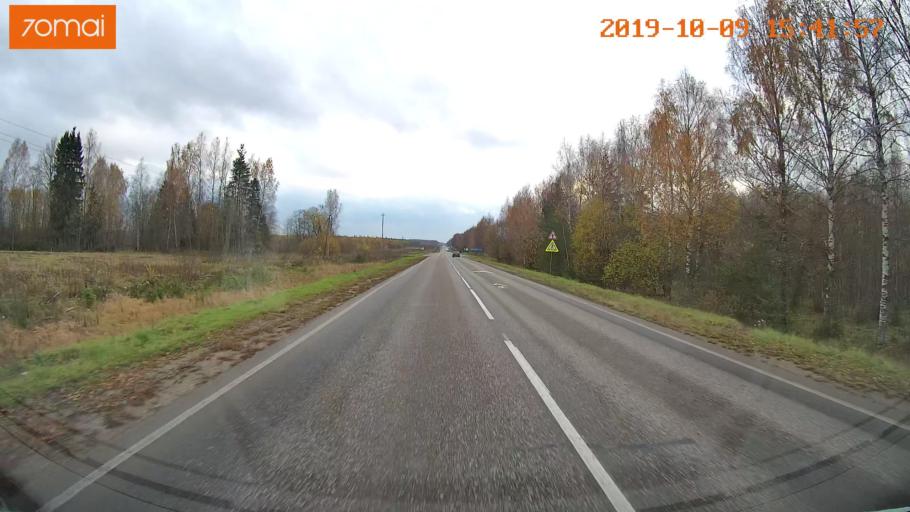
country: RU
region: Kostroma
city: Oktyabr'skiy
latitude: 57.8735
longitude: 41.1158
